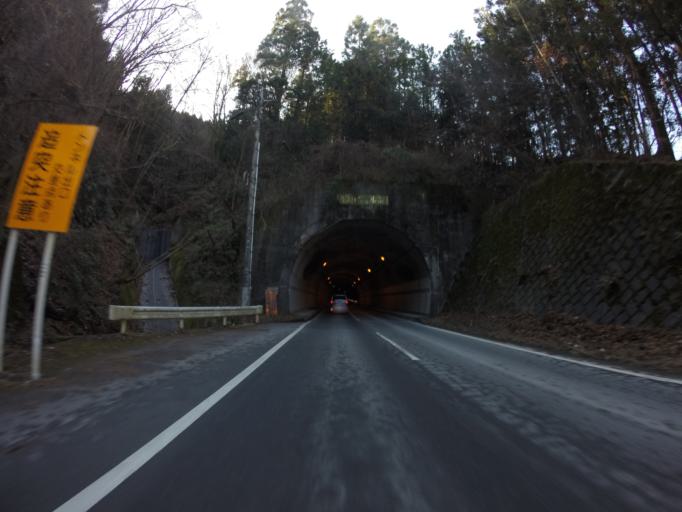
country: JP
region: Yamanashi
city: Ryuo
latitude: 35.4114
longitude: 138.3725
